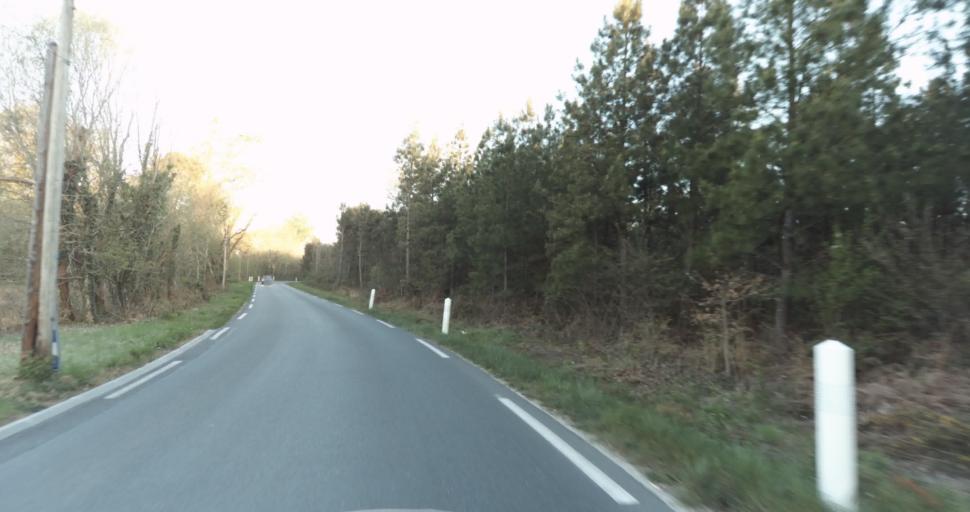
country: FR
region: Aquitaine
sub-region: Departement de la Gironde
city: Martignas-sur-Jalle
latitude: 44.8178
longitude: -0.7512
